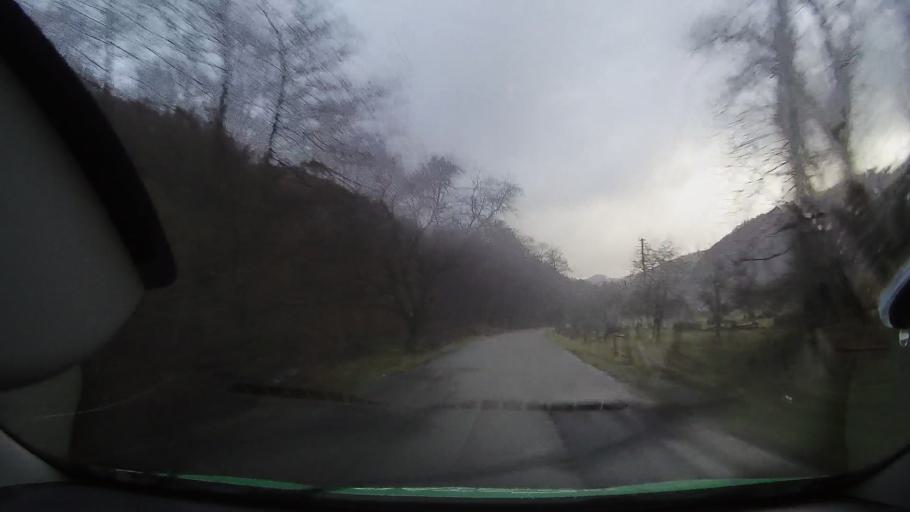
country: RO
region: Hunedoara
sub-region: Comuna Ribita
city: Ribita
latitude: 46.2654
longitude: 22.7422
